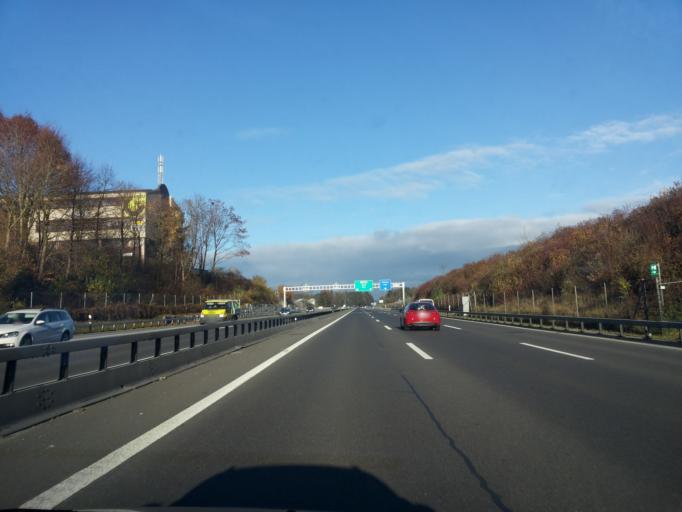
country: CH
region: Lucerne
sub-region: Hochdorf District
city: Emmen
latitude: 47.0857
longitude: 8.2564
